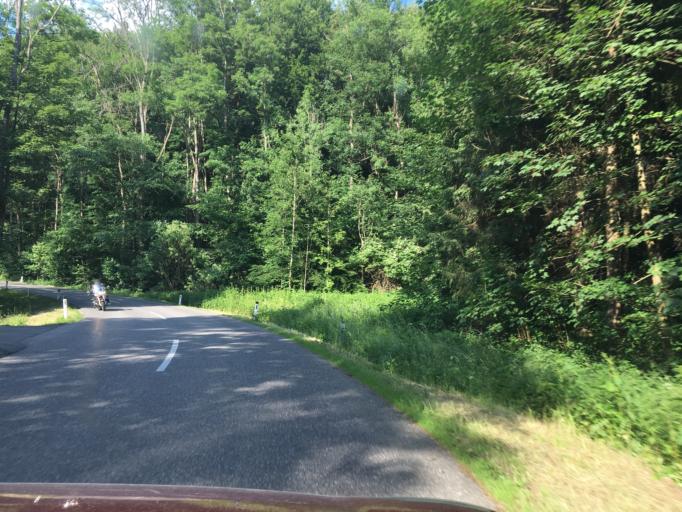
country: AT
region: Upper Austria
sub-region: Politischer Bezirk Urfahr-Umgebung
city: Alberndorf in der Riedmark
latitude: 48.3939
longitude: 14.4023
